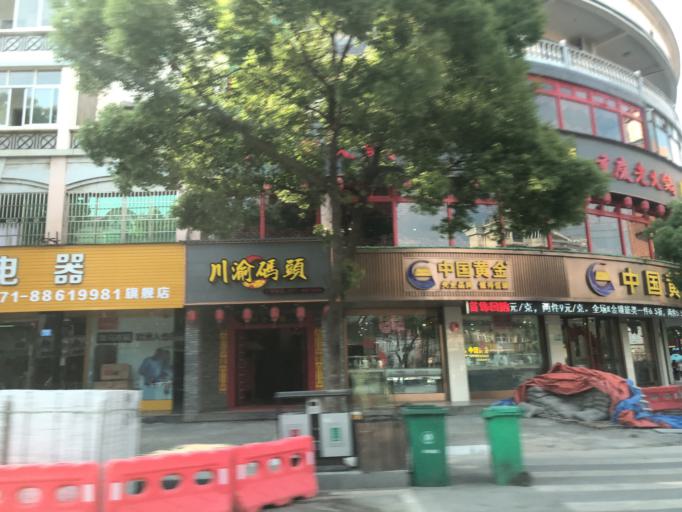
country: CN
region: Zhejiang Sheng
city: Qiaosi
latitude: 30.3503
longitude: 120.2858
